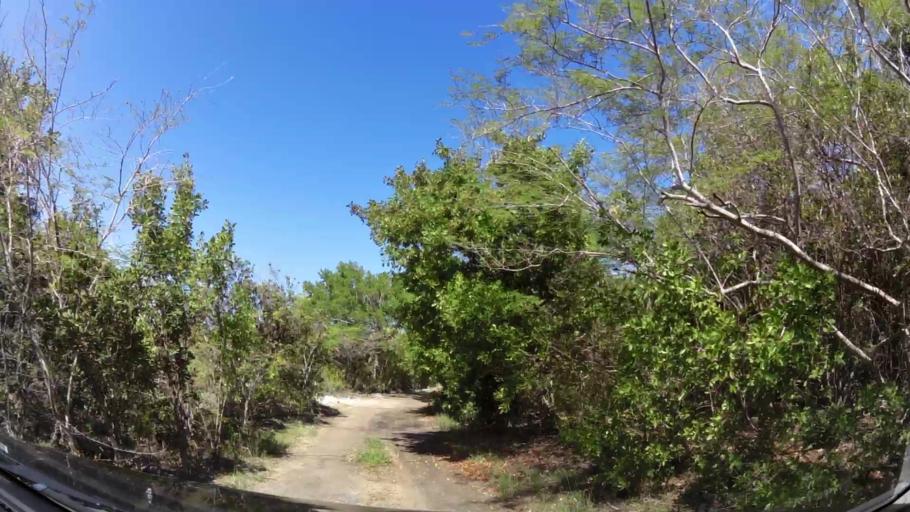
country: VG
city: Tortola
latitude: 18.4475
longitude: -64.5280
